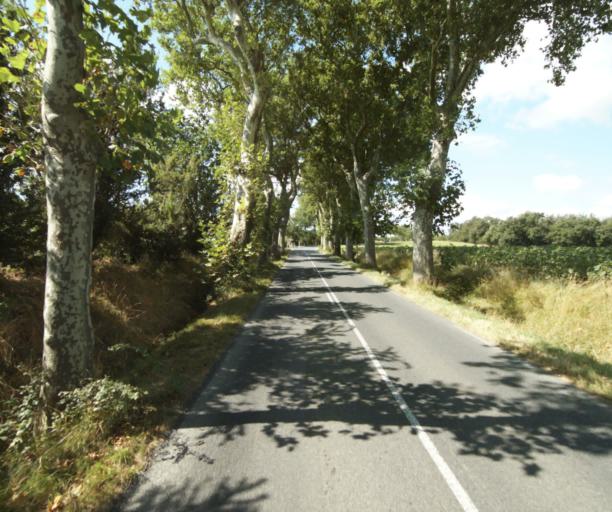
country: FR
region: Midi-Pyrenees
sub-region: Departement de la Haute-Garonne
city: Avignonet-Lauragais
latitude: 43.4450
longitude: 1.7906
